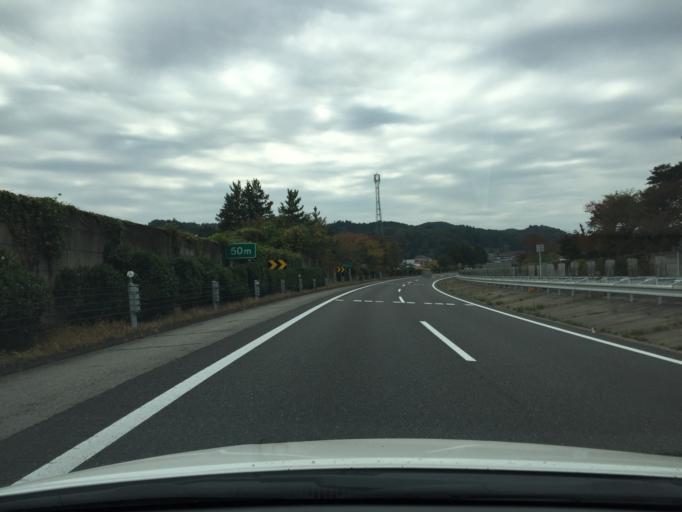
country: JP
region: Fukushima
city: Sukagawa
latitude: 37.1633
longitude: 140.2684
